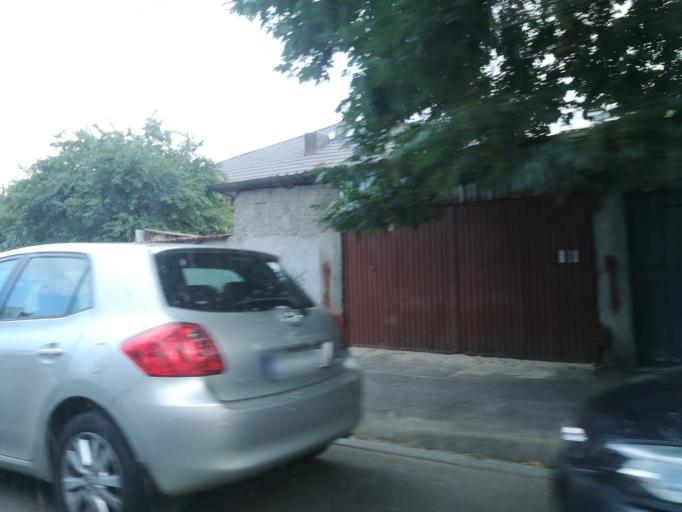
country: RO
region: Ilfov
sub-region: Comuna Chiajna
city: Rosu
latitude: 44.4899
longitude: 26.0460
